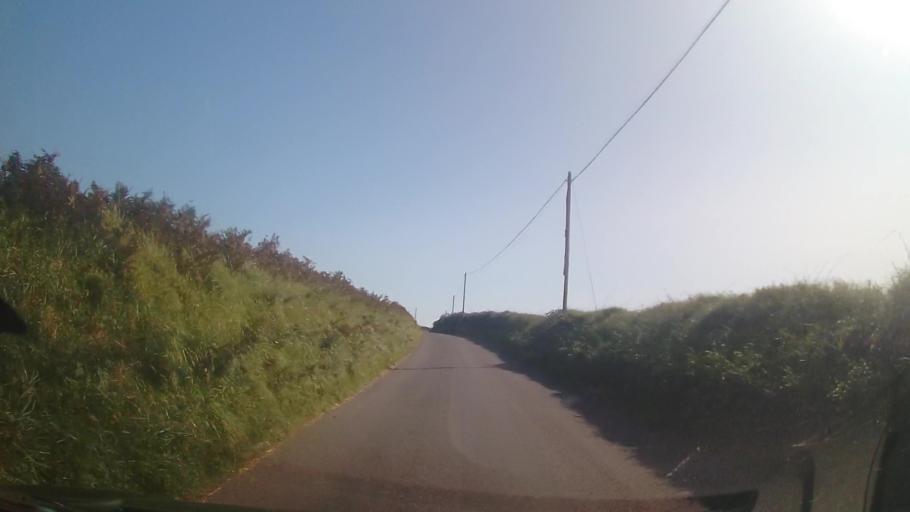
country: GB
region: Wales
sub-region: Pembrokeshire
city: Llanrhian
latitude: 51.9343
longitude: -5.1692
